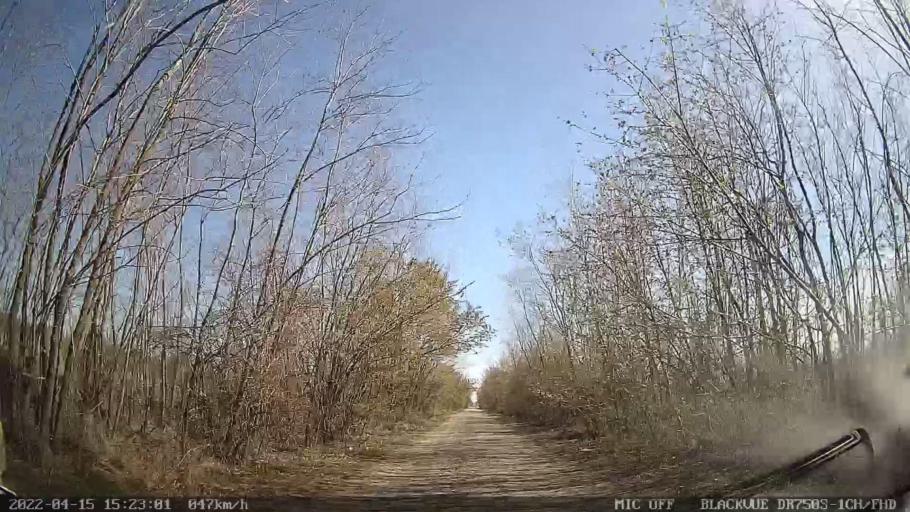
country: MD
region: Raionul Ocnita
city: Otaci
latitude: 48.3776
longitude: 27.9174
